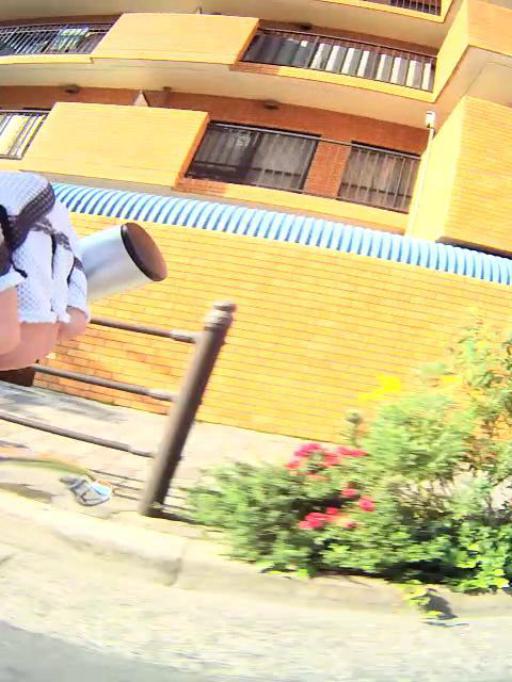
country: JP
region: Osaka
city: Suita
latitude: 34.7336
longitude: 135.4943
